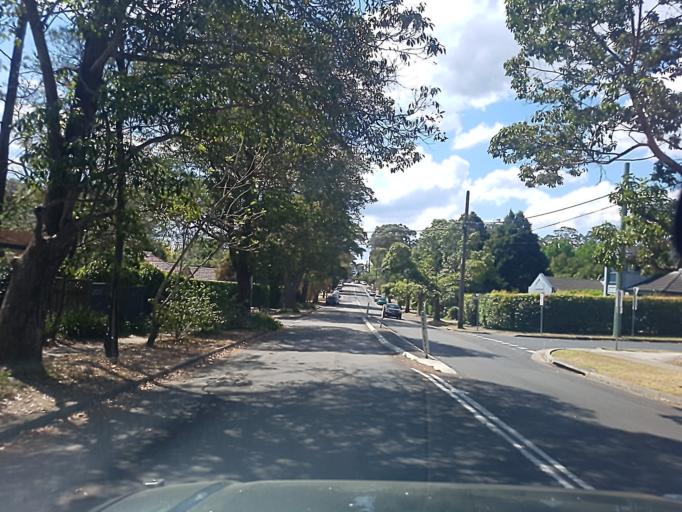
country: AU
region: New South Wales
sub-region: Hornsby Shire
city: Hornsby
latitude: -33.7102
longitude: 151.1100
